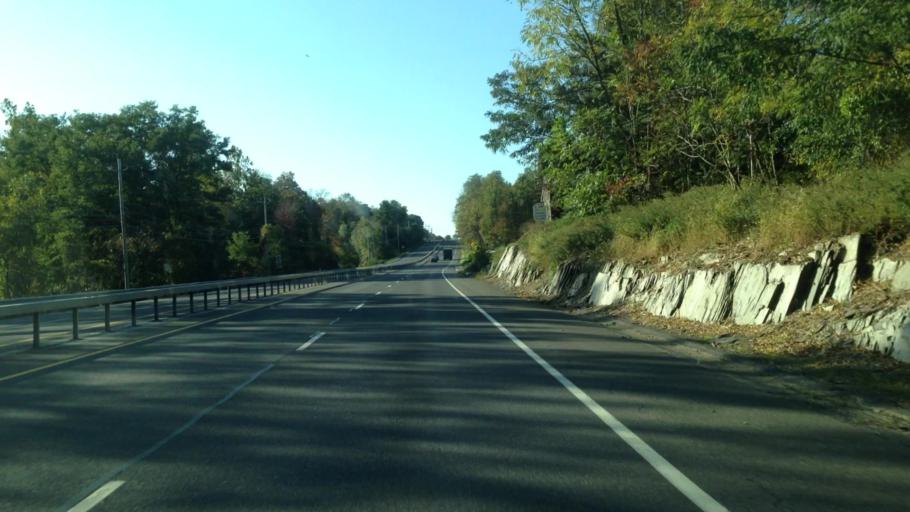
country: US
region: New York
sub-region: Dutchess County
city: Hyde Park
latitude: 41.7657
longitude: -73.9608
